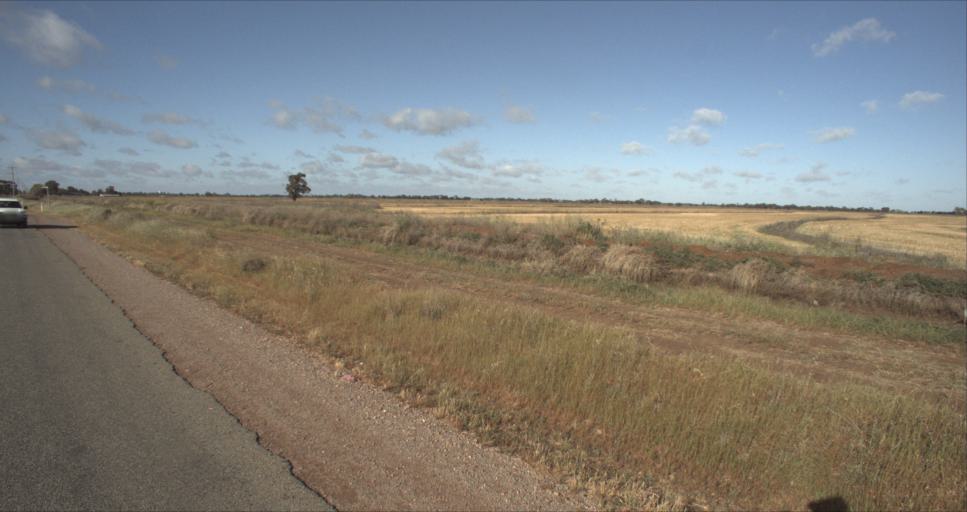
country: AU
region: New South Wales
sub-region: Leeton
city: Leeton
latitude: -34.5104
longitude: 146.3924
